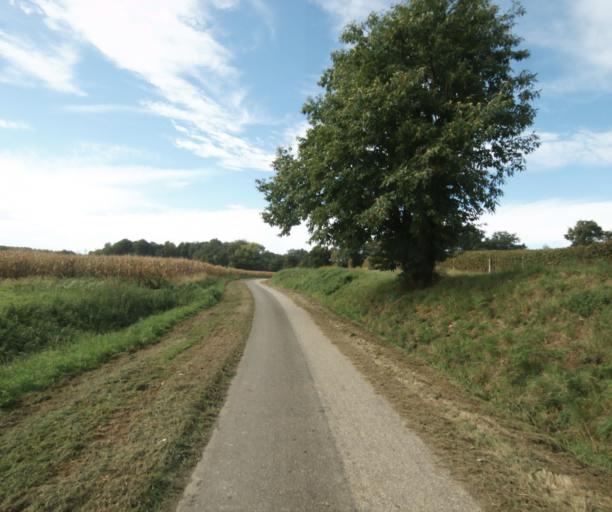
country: FR
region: Aquitaine
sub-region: Departement des Landes
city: Villeneuve-de-Marsan
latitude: 43.8975
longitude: -0.2081
